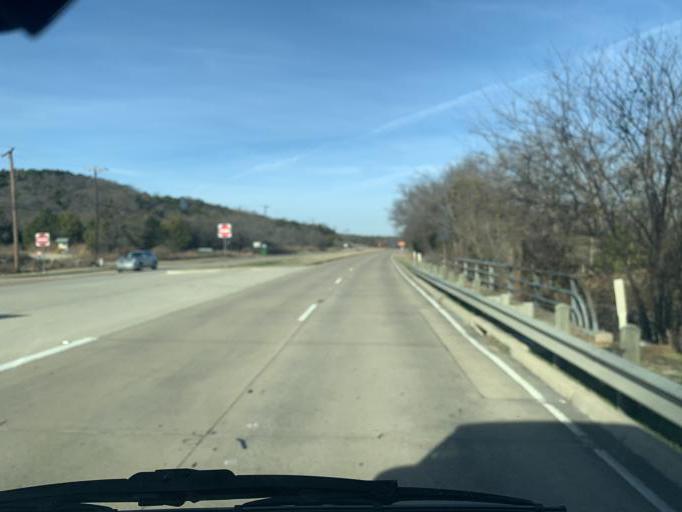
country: US
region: Texas
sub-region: Dallas County
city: Cedar Hill
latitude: 32.6144
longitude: -96.9692
